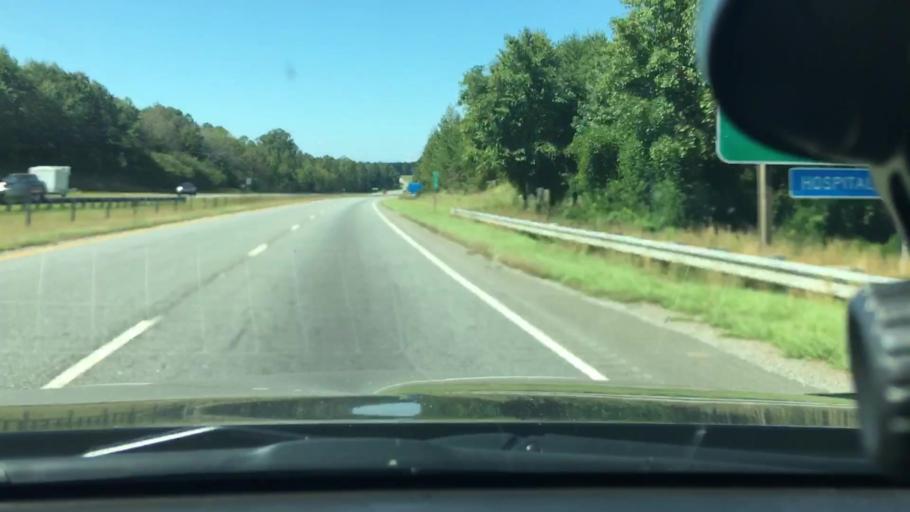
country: US
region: North Carolina
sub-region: Rutherford County
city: Forest City
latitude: 35.3070
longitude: -81.9087
